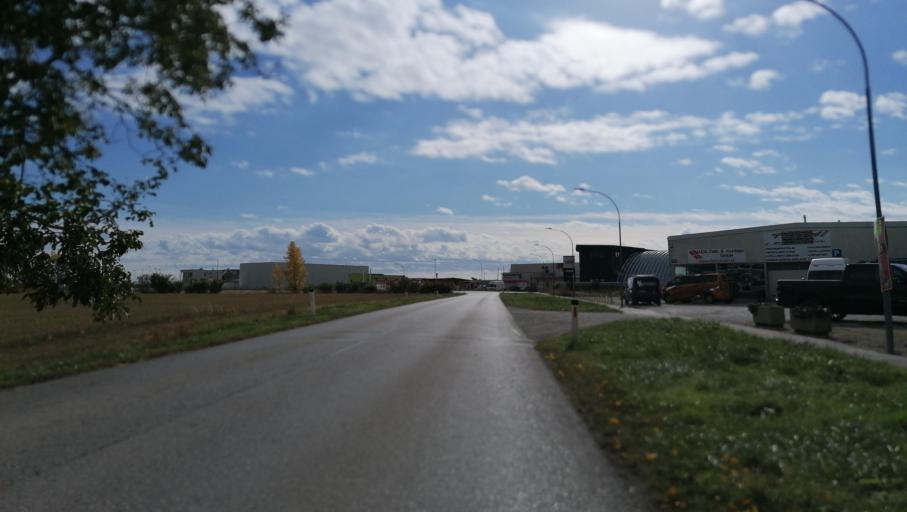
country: AT
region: Lower Austria
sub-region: Politischer Bezirk Baden
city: Teesdorf
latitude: 47.9767
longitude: 16.2782
